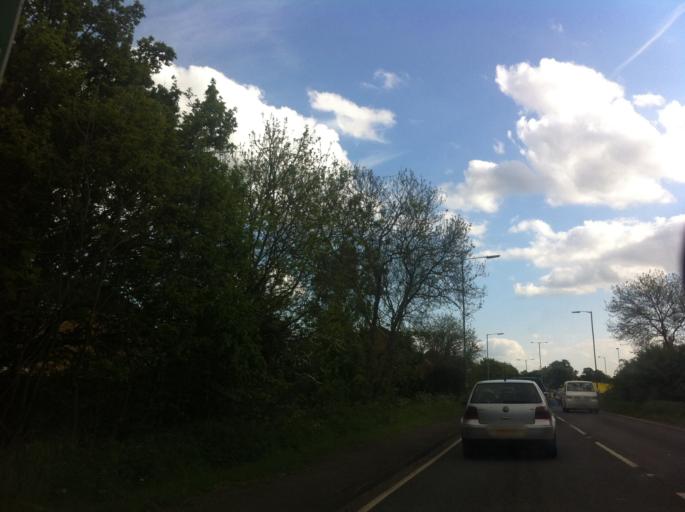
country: GB
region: England
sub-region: Northamptonshire
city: Bozeat
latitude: 52.2595
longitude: -0.6778
